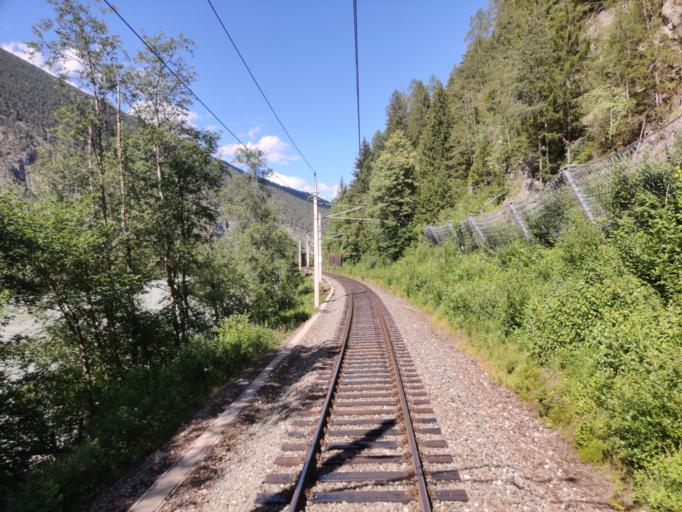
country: AT
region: Tyrol
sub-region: Politischer Bezirk Imst
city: Imsterberg
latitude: 47.2046
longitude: 10.6880
